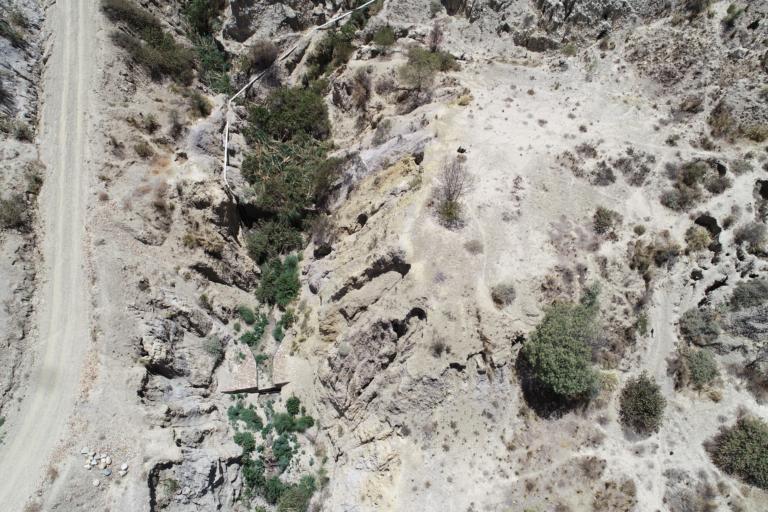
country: BO
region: La Paz
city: La Paz
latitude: -16.5204
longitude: -68.0766
